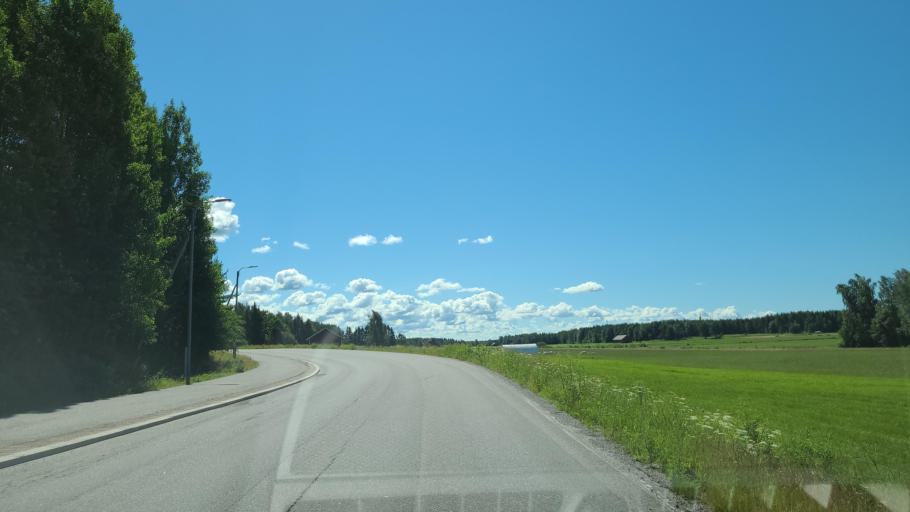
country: FI
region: Ostrobothnia
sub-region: Vaasa
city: Ristinummi
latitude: 63.0661
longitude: 21.7242
